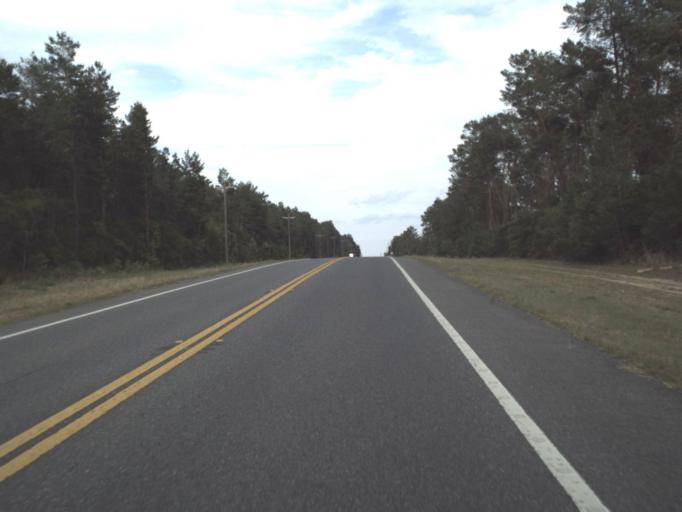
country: US
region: Florida
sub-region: Lake County
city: Astor
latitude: 29.1772
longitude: -81.7779
